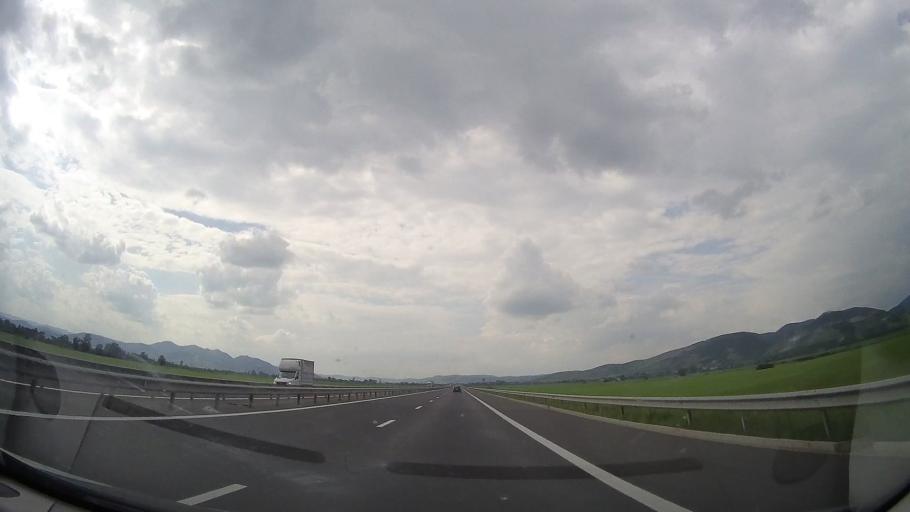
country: RO
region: Hunedoara
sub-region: Oras Simeria
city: Simeria
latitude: 45.8749
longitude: 23.0068
